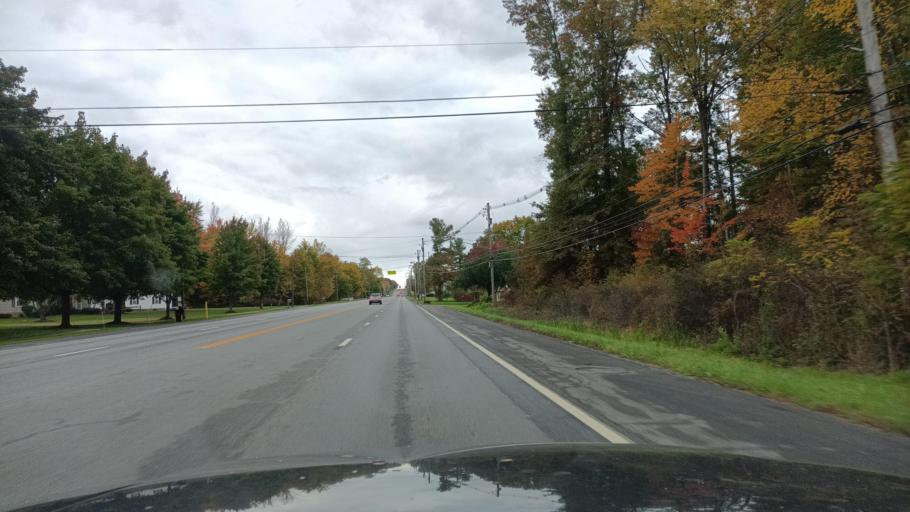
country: US
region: Ohio
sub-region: Trumbull County
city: Lordstown
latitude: 41.1717
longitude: -80.8574
